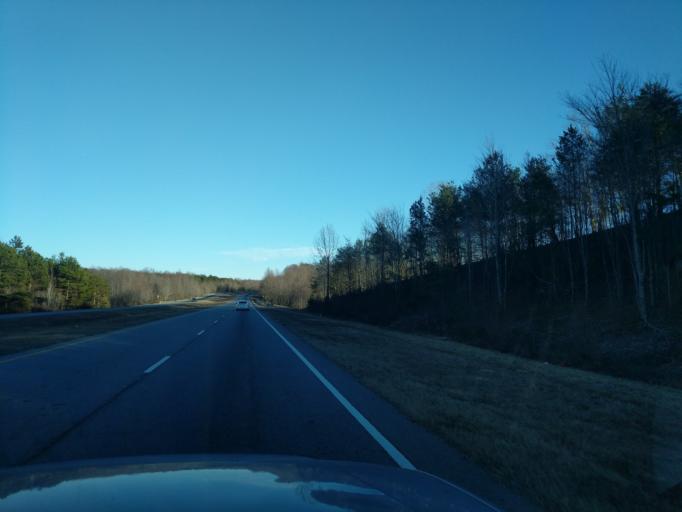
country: US
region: Georgia
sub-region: Stephens County
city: Toccoa
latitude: 34.5938
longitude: -83.4254
